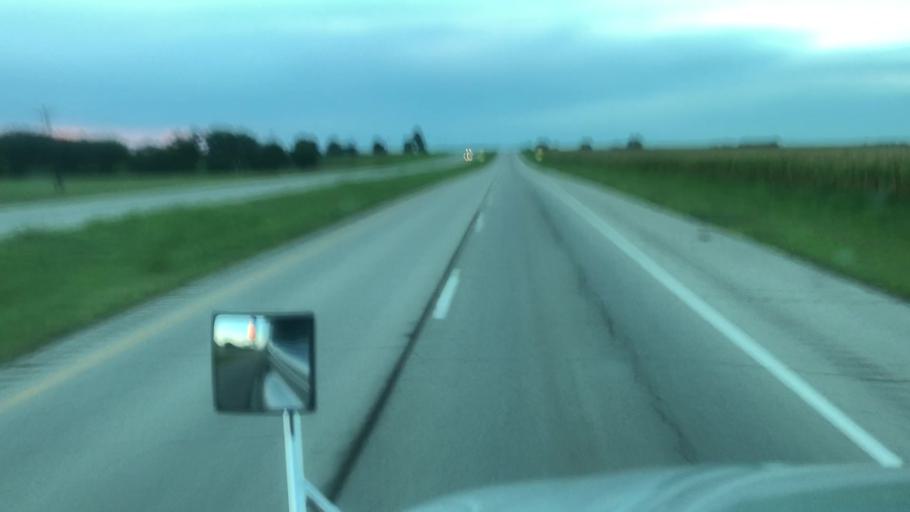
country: US
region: Oklahoma
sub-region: Kay County
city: Newkirk
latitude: 36.7969
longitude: -97.0672
